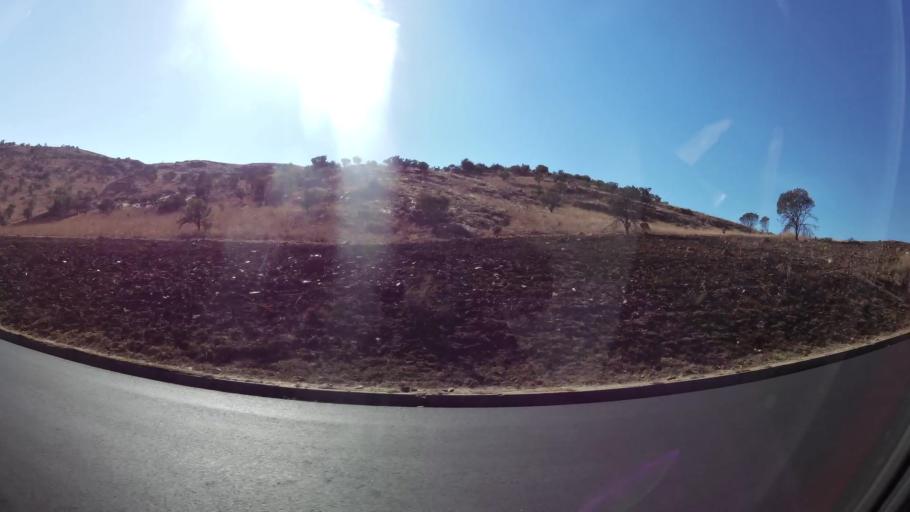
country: ZA
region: Gauteng
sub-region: City of Johannesburg Metropolitan Municipality
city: Roodepoort
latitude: -26.1283
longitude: 27.8837
